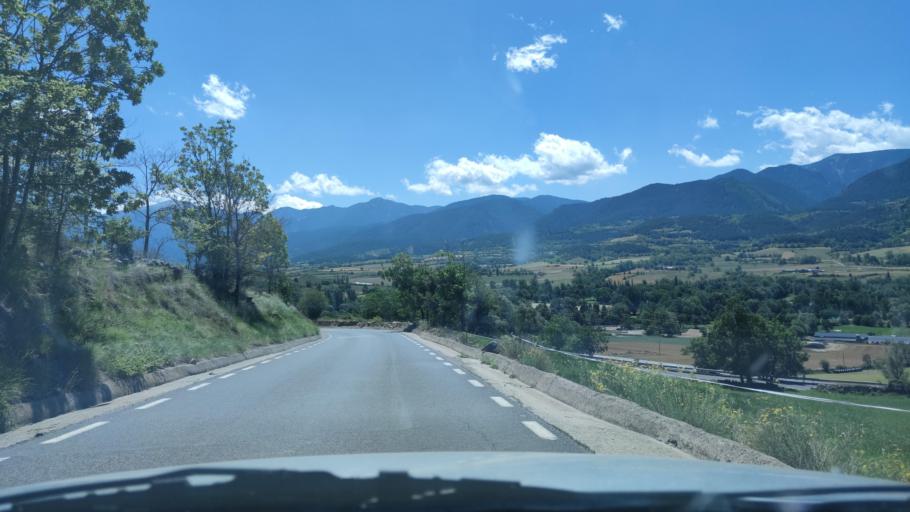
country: ES
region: Catalonia
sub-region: Provincia de Lleida
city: Bellver de Cerdanya
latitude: 42.3752
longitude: 1.7423
